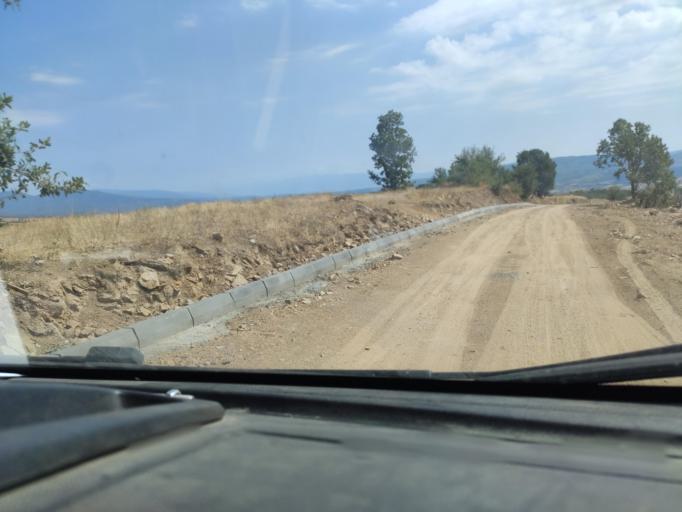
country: MK
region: Radovis
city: Radovish
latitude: 41.6743
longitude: 22.4040
